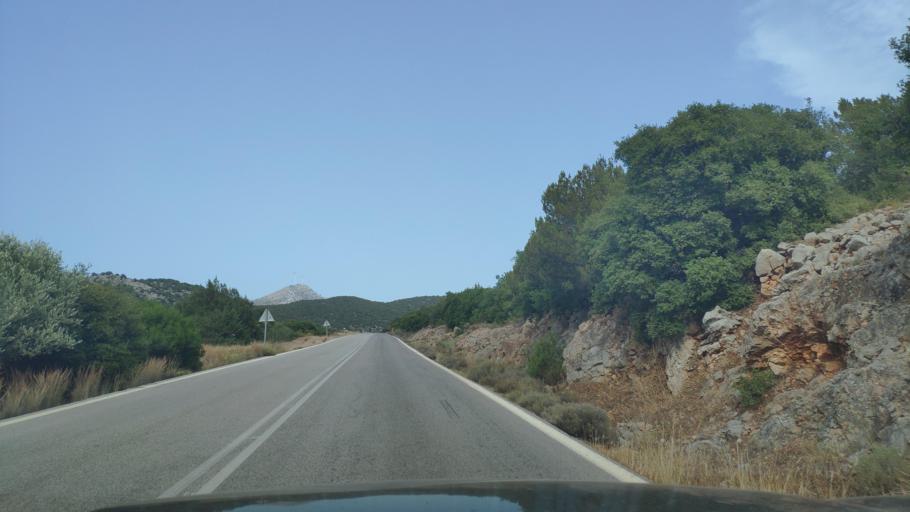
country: GR
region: Peloponnese
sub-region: Nomos Argolidos
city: Didyma
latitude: 37.5102
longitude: 23.1966
